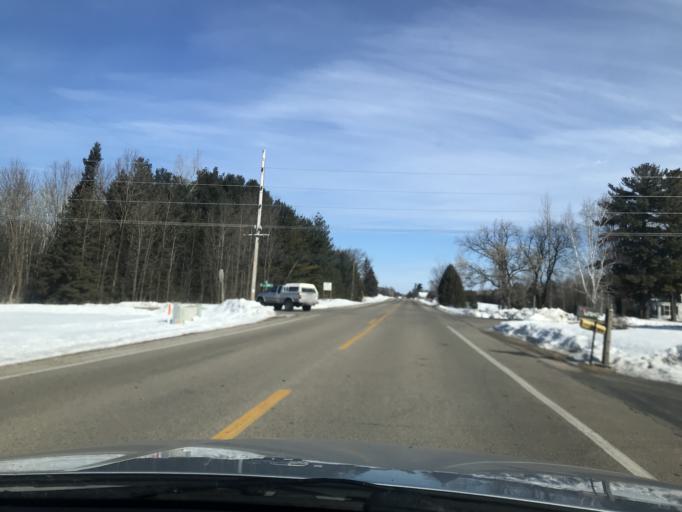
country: US
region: Wisconsin
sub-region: Oconto County
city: Oconto Falls
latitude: 44.9078
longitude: -88.1552
